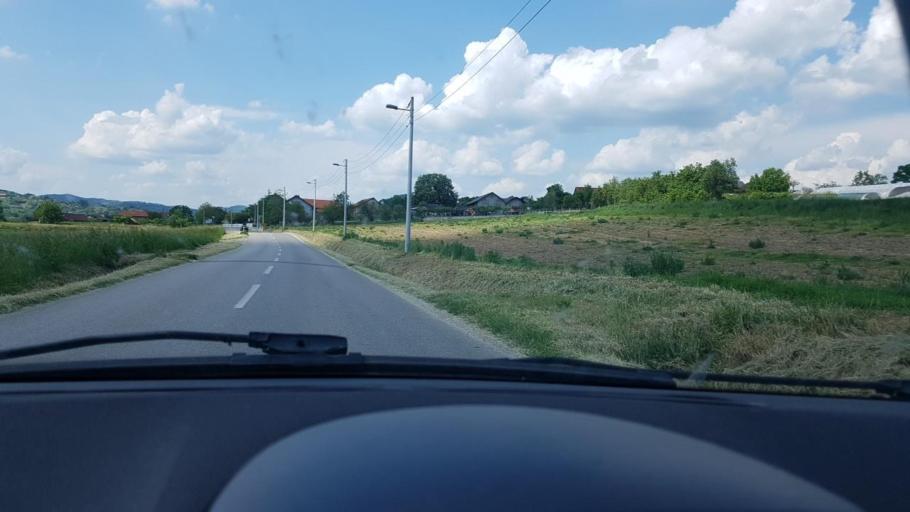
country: HR
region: Grad Zagreb
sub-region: Sesvete
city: Sesvete
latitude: 45.8925
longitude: 16.1704
